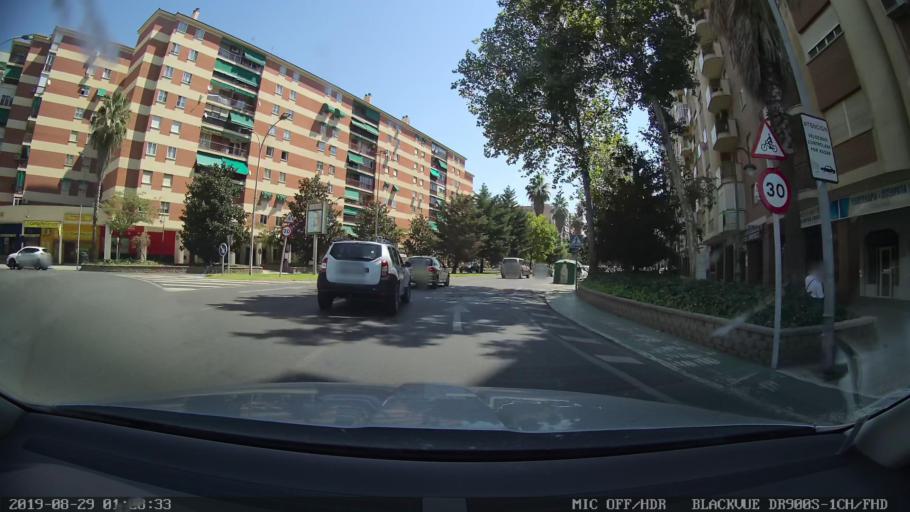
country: ES
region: Extremadura
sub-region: Provincia de Badajoz
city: Badajoz
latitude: 38.8717
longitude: -6.9898
